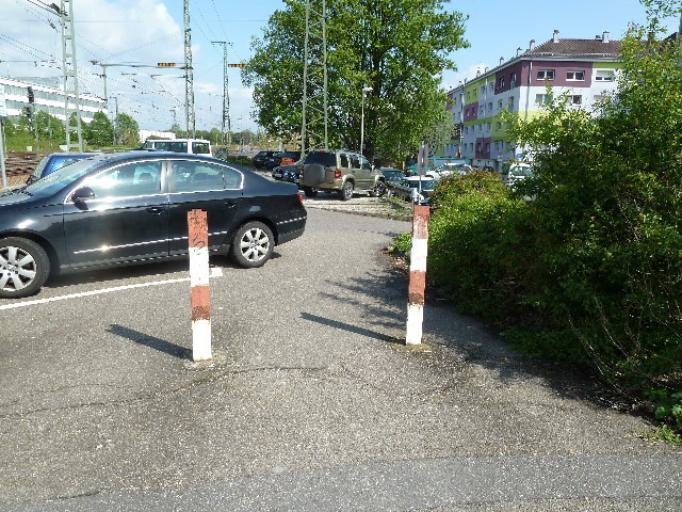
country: DE
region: Baden-Wuerttemberg
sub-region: Karlsruhe Region
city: Bruchsal
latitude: 49.1259
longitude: 8.5910
